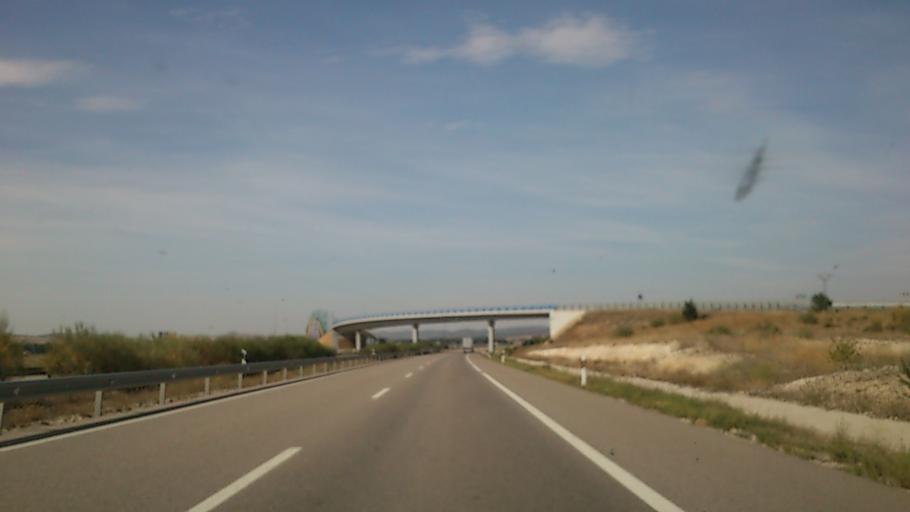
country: ES
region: Aragon
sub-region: Provincia de Teruel
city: Fuentes Claras
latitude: 40.8852
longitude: -1.3059
